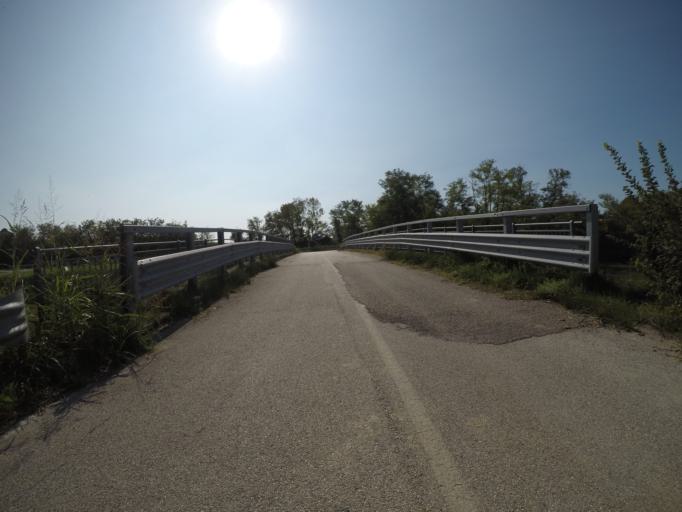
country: IT
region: Veneto
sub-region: Provincia di Rovigo
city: Polesella
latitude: 44.9622
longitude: 11.7374
